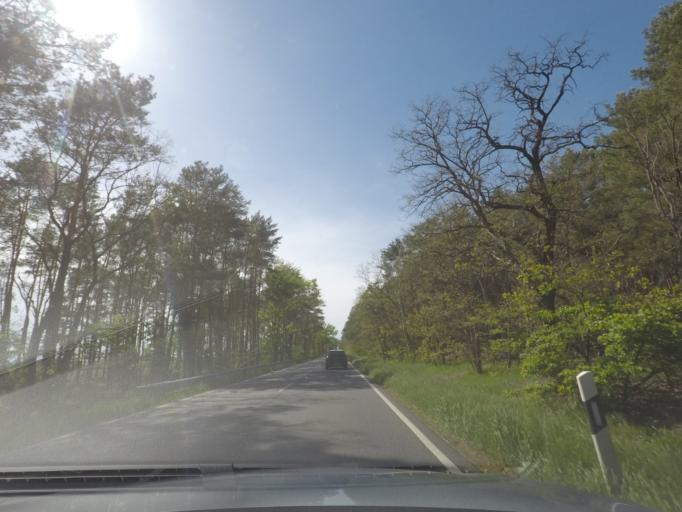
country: DE
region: Brandenburg
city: Kasel-Golzig
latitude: 51.9514
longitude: 13.7820
